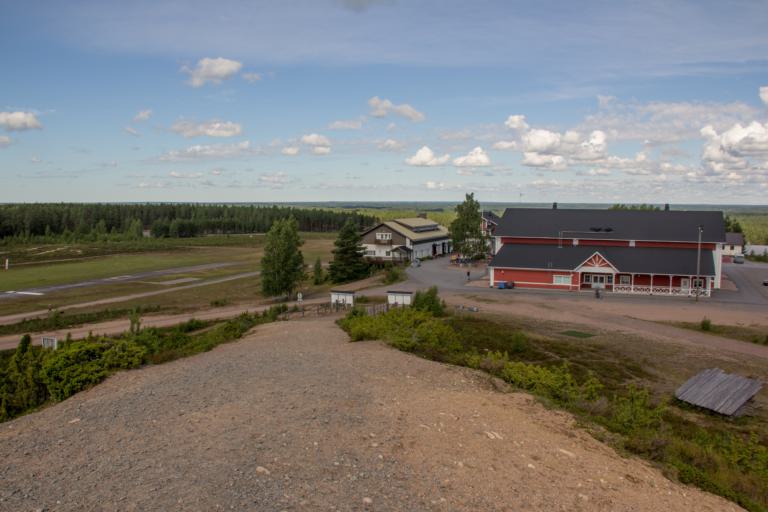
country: FI
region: Satakunta
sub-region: Pohjois-Satakunta
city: Jaemijaervi
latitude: 61.7772
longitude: 22.7163
